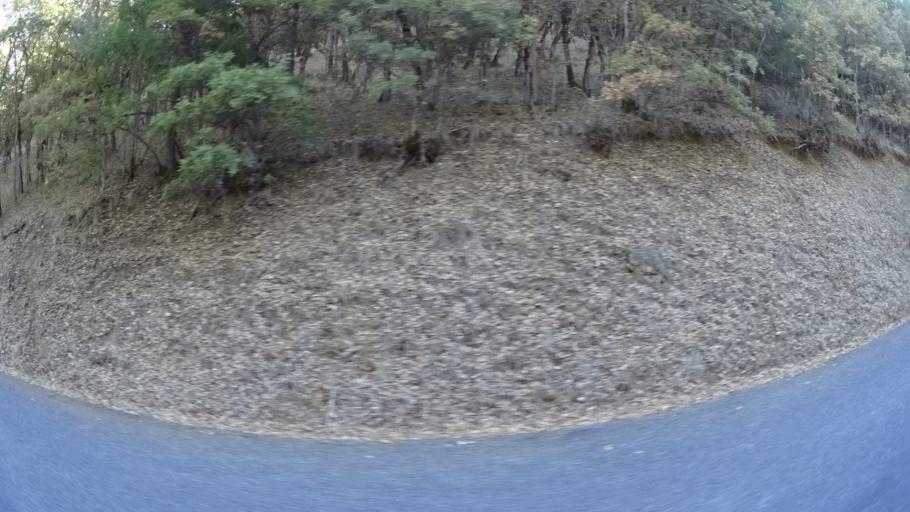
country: US
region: California
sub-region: Trinity County
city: Weaverville
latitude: 41.1511
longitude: -123.1105
